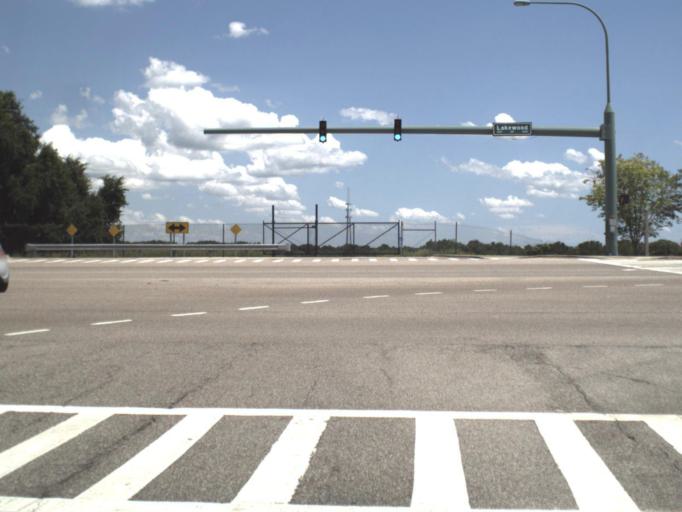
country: US
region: Florida
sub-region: Hillsborough County
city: Brandon
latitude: 27.9305
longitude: -82.3109
